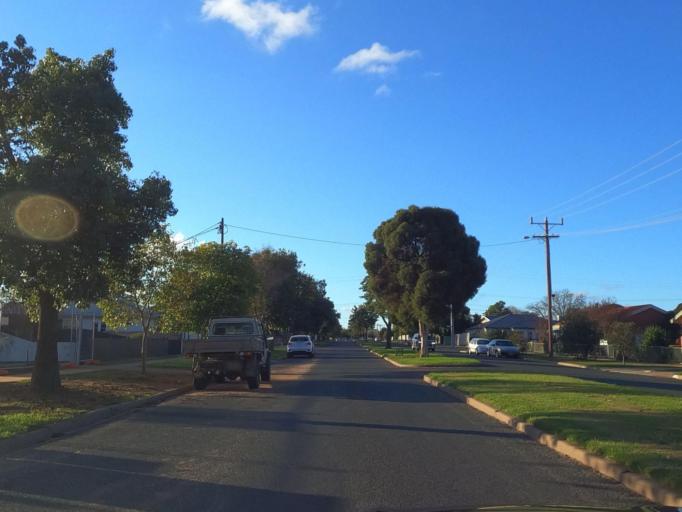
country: AU
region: Victoria
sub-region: Swan Hill
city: Swan Hill
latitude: -35.3473
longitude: 143.5554
